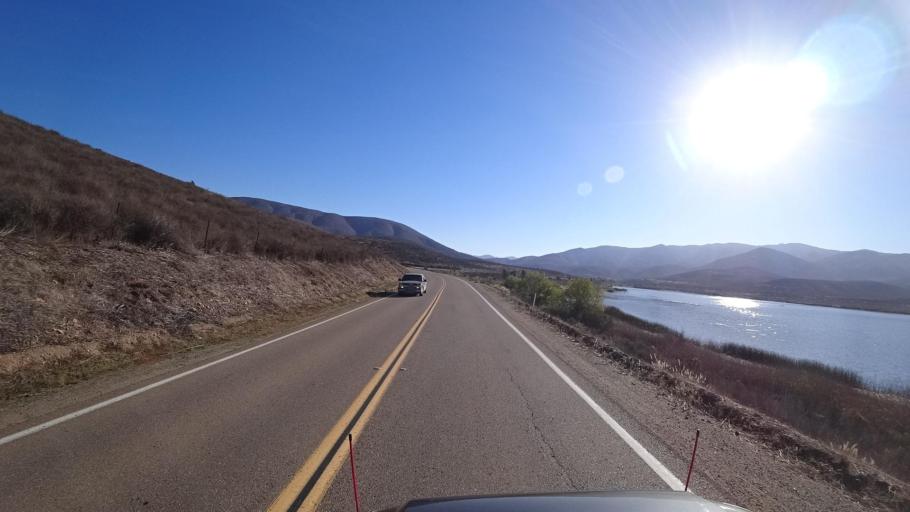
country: US
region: California
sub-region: San Diego County
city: Jamul
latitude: 32.6344
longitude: -116.9144
